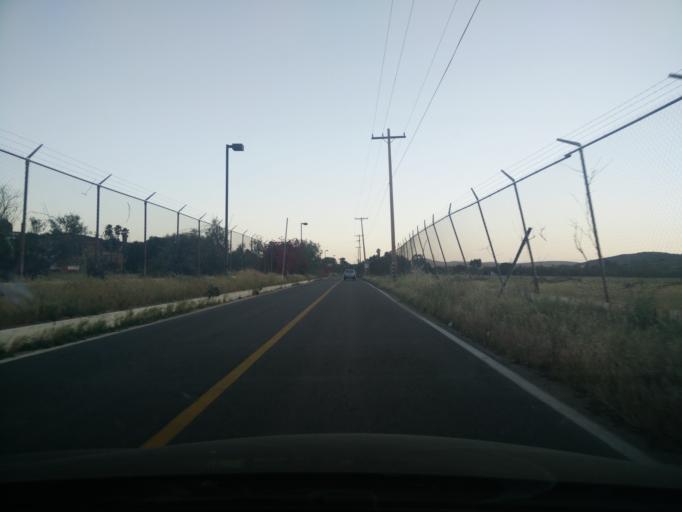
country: MX
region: Baja California
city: El Sauzal
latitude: 32.0312
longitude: -116.6733
